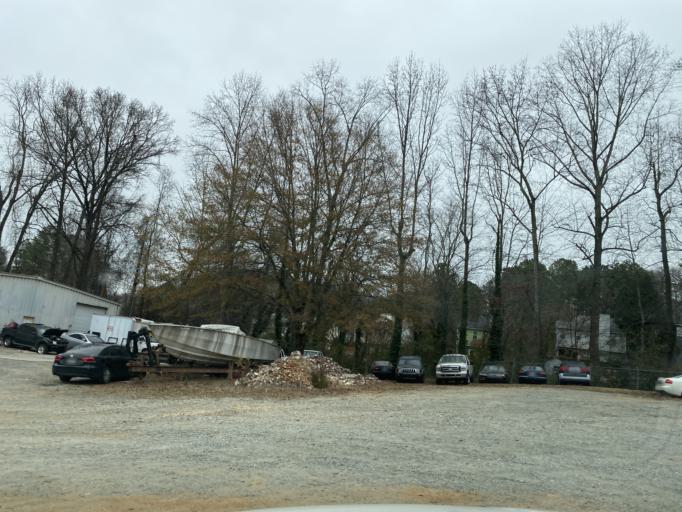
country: US
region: Georgia
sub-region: Cobb County
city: Fair Oaks
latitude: 33.9074
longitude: -84.5711
